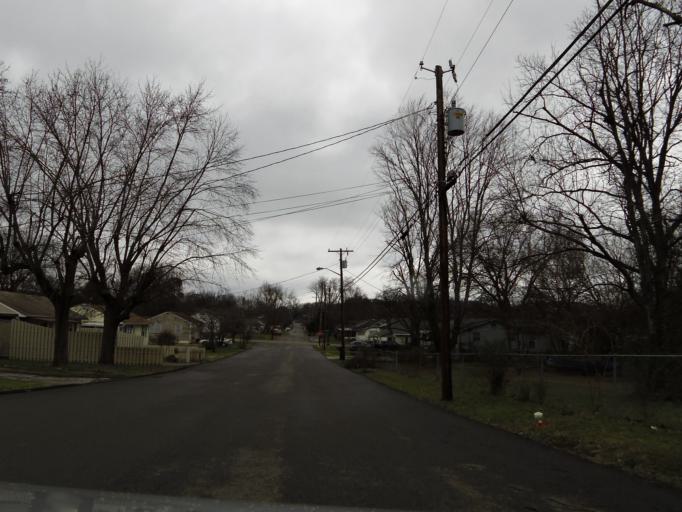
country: US
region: Tennessee
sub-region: Knox County
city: Knoxville
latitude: 35.9704
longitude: -83.9722
